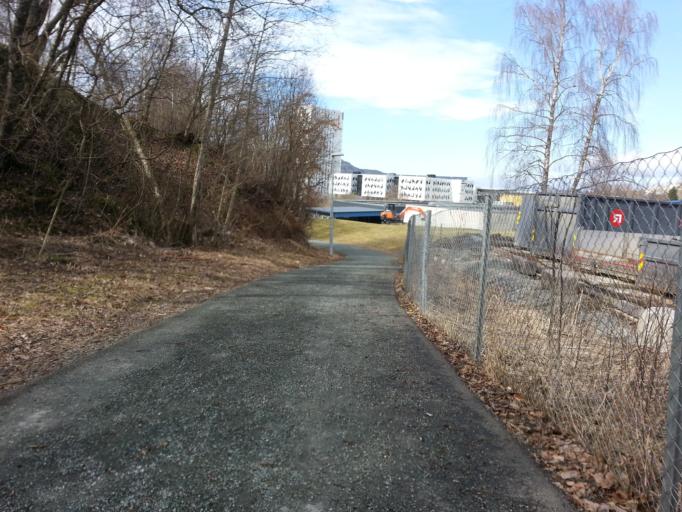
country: NO
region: Sor-Trondelag
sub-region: Trondheim
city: Trondheim
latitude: 63.4092
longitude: 10.4096
